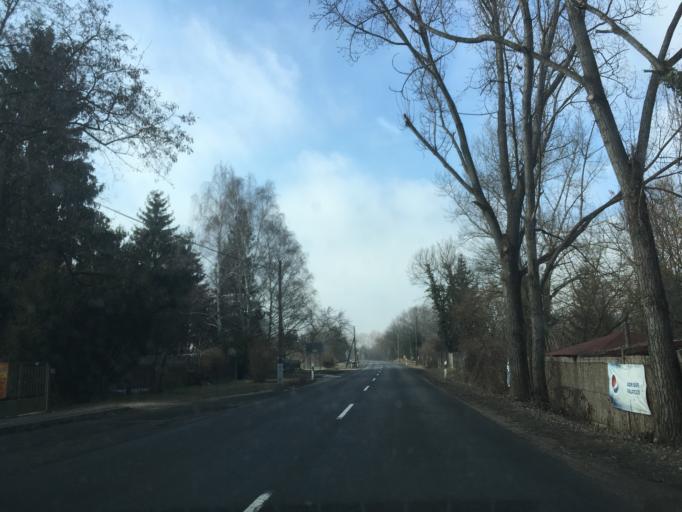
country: HU
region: Komarom-Esztergom
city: Esztergom
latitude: 47.8147
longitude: 18.7923
